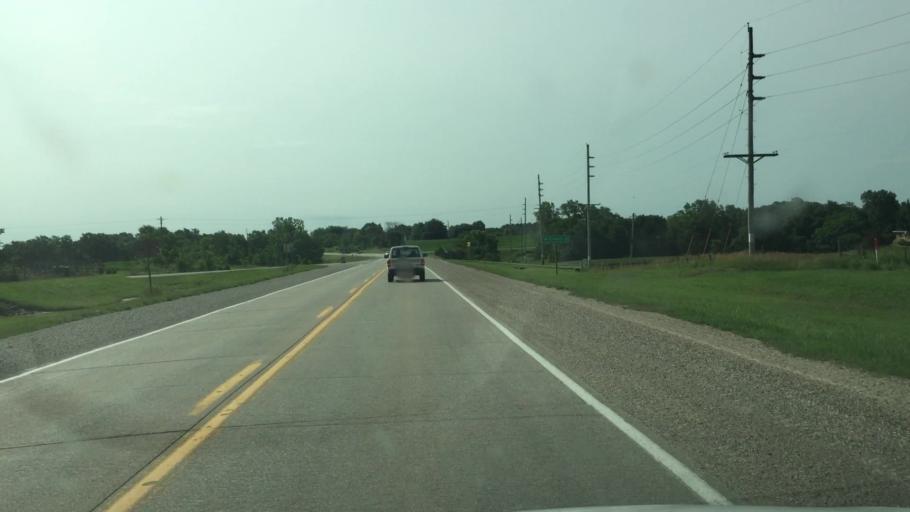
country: US
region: Illinois
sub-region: Hancock County
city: Nauvoo
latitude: 40.6361
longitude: -91.5184
